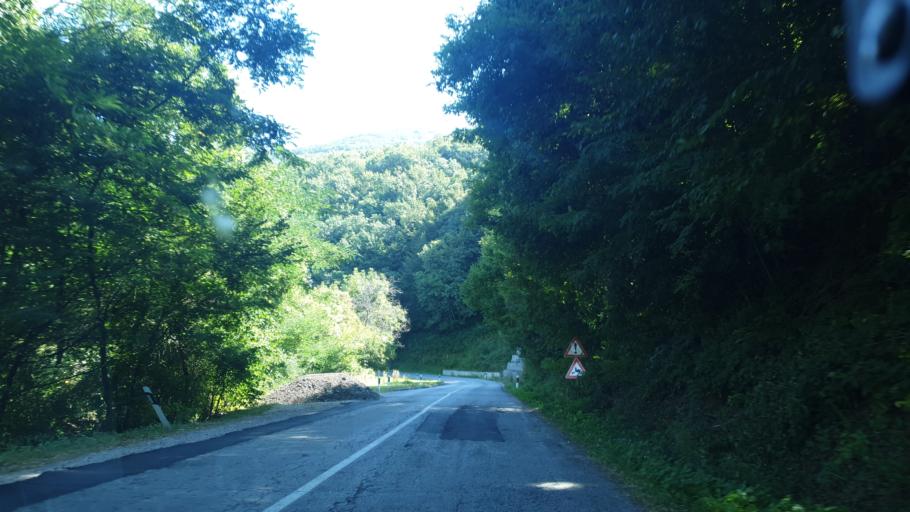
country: RS
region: Central Serbia
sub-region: Kolubarski Okrug
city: Mionica
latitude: 44.1551
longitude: 19.9968
